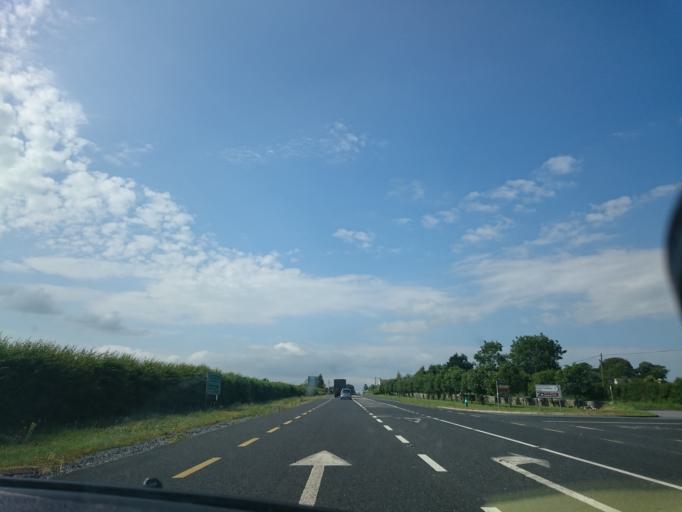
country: IE
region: Leinster
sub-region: Kilkenny
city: Kilkenny
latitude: 52.5801
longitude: -7.2373
